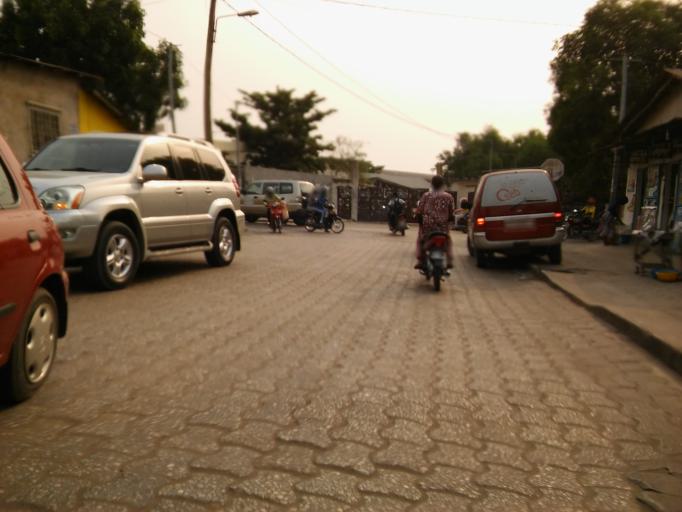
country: BJ
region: Littoral
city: Cotonou
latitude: 6.3602
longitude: 2.4058
